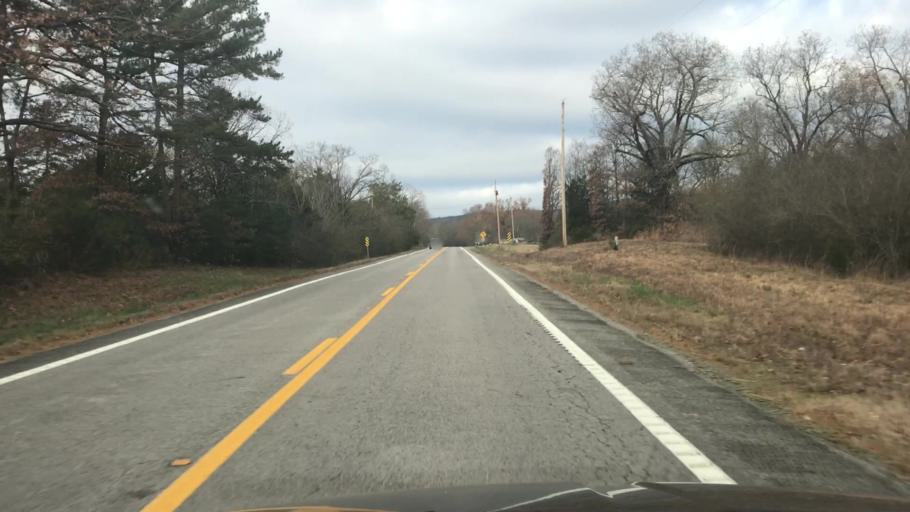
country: US
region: Arkansas
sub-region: Montgomery County
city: Mount Ida
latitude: 34.6558
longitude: -93.7591
